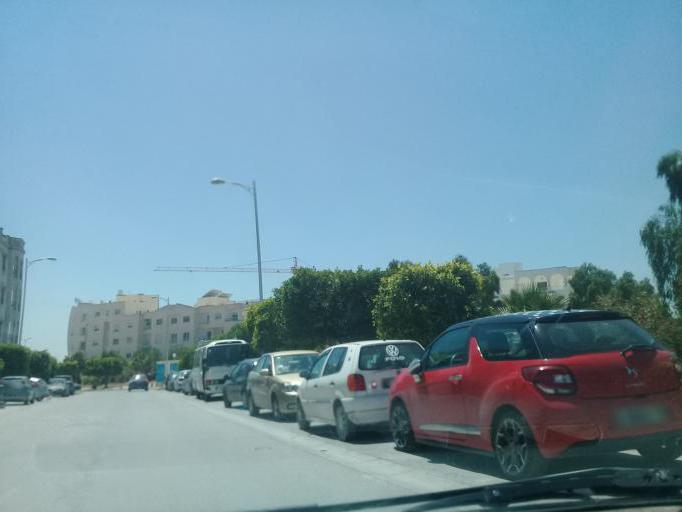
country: TN
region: Tunis
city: La Goulette
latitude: 36.8443
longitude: 10.2778
